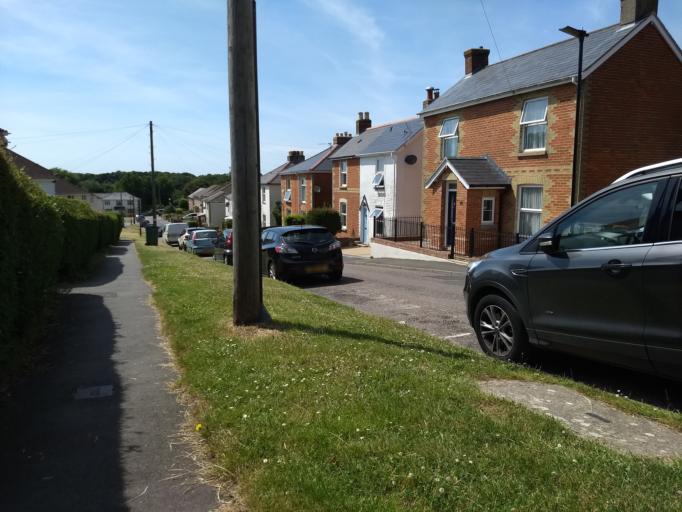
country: GB
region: England
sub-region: Isle of Wight
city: Ryde
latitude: 50.7173
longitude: -1.1762
